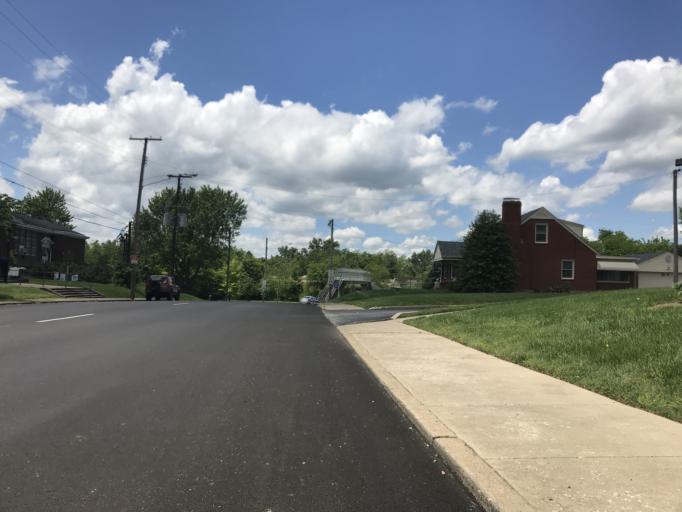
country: US
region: Kentucky
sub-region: Jefferson County
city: Shively
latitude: 38.2393
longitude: -85.8138
